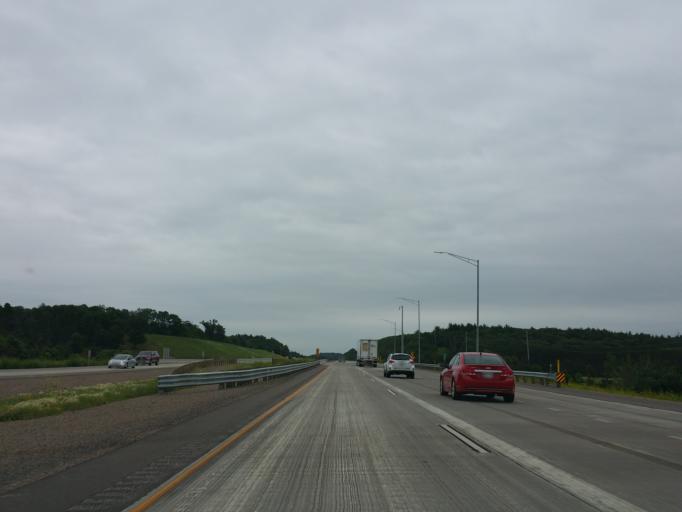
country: US
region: Wisconsin
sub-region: Eau Claire County
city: Eau Claire
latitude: 44.7794
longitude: -91.5347
